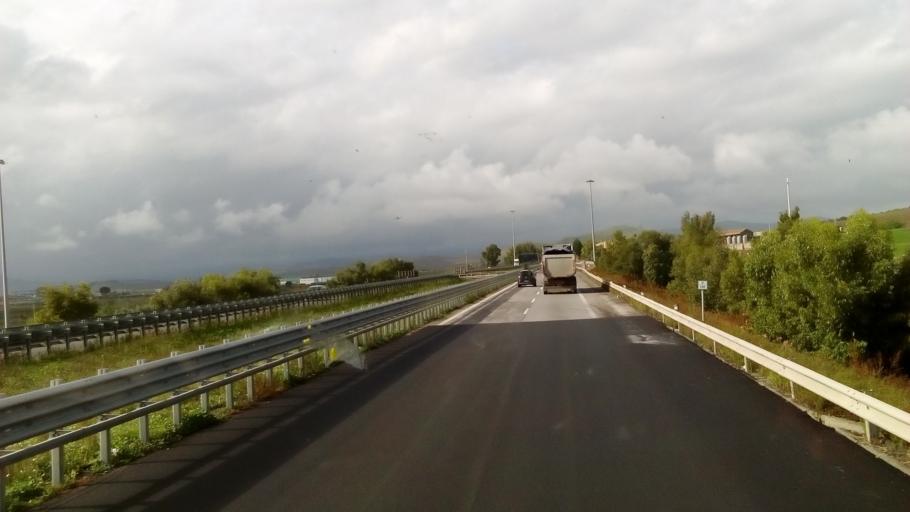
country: IT
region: Sicily
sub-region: Enna
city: Assoro
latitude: 37.5708
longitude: 14.4779
